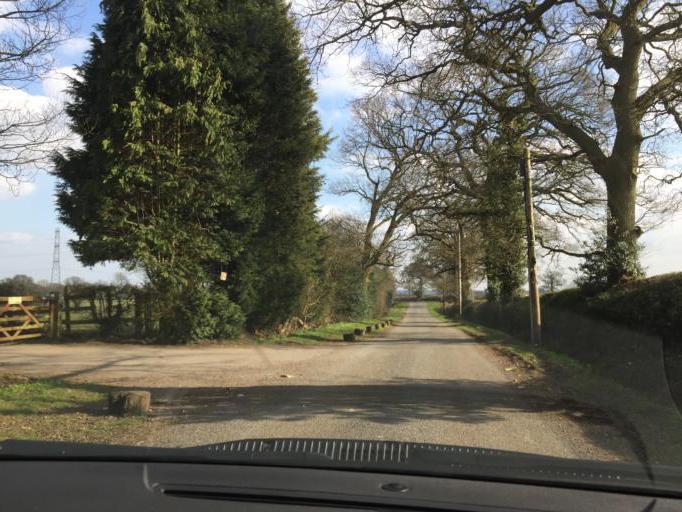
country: GB
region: England
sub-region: Coventry
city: Keresley
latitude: 52.4477
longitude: -1.5844
